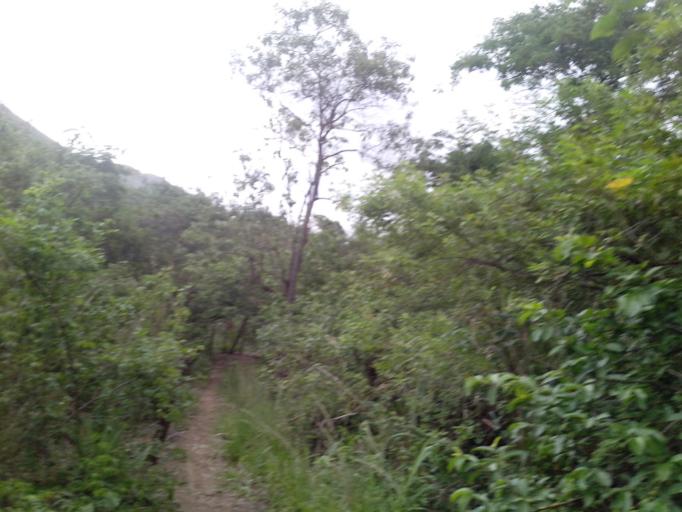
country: BR
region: Rio de Janeiro
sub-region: Miguel Pereira
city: Miguel Pereira
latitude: -22.5089
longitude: -43.5162
